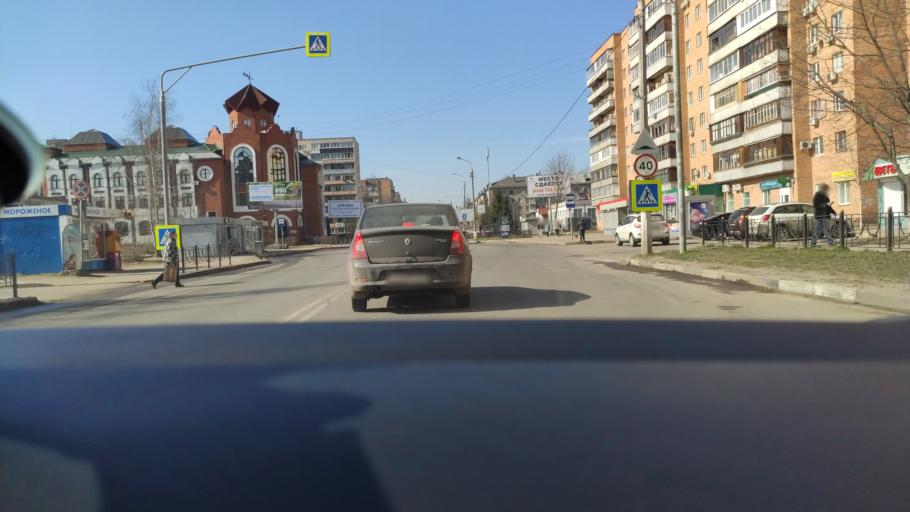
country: RU
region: Moskovskaya
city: Elektrostal'
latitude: 55.7708
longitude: 38.4451
